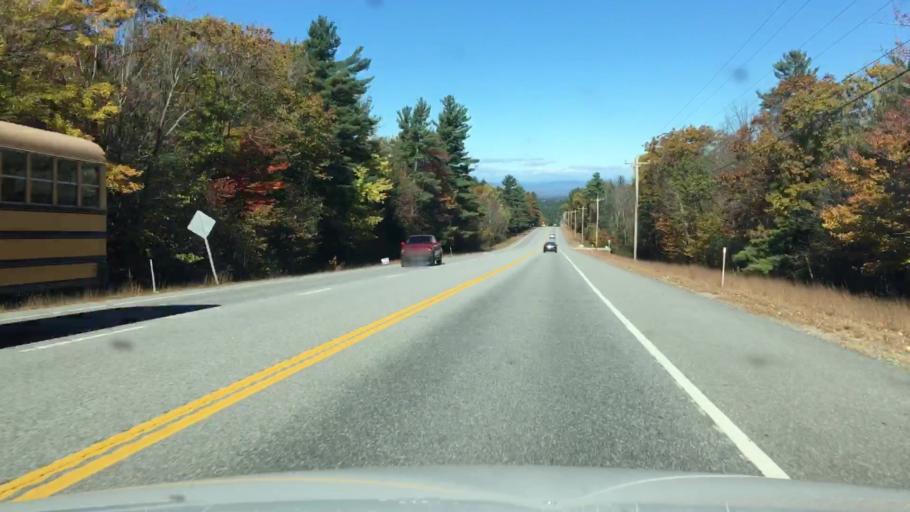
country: US
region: New Hampshire
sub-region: Carroll County
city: Wakefield
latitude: 43.6187
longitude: -71.0423
